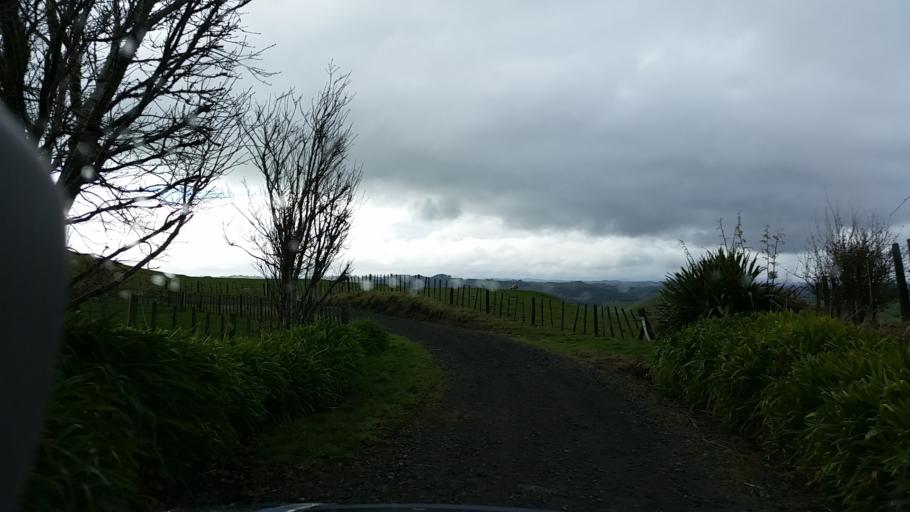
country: NZ
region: Taranaki
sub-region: South Taranaki District
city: Eltham
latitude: -39.2758
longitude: 174.3396
